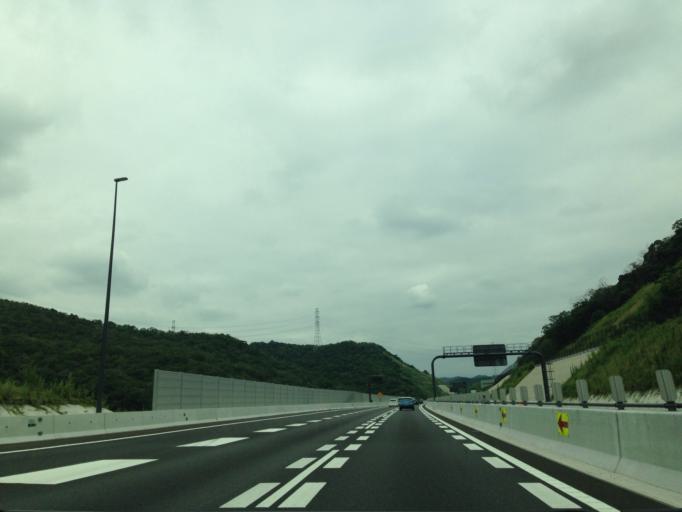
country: JP
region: Aichi
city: Gamagori
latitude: 34.9221
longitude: 137.2734
